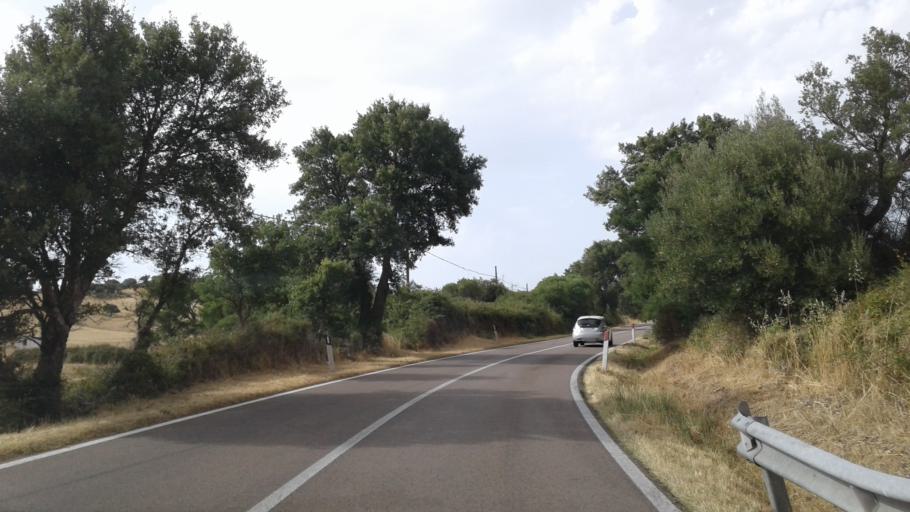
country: IT
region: Sardinia
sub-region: Provincia di Olbia-Tempio
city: Sant'Antonio di Gallura
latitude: 40.9520
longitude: 9.2943
